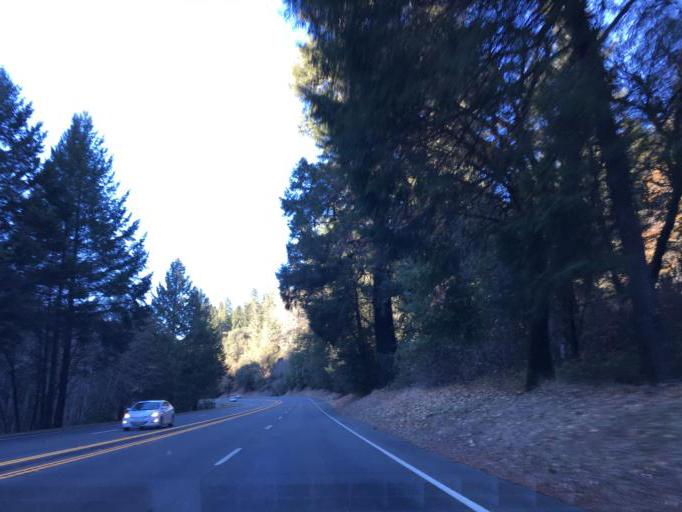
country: US
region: California
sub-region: Mendocino County
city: Laytonville
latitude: 39.5771
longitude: -123.4399
